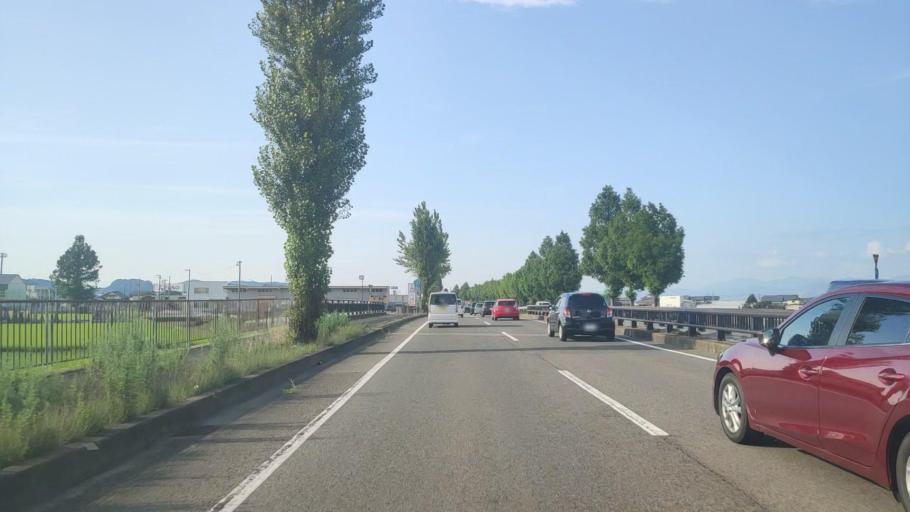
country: JP
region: Fukui
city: Sabae
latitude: 36.0040
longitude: 136.2081
